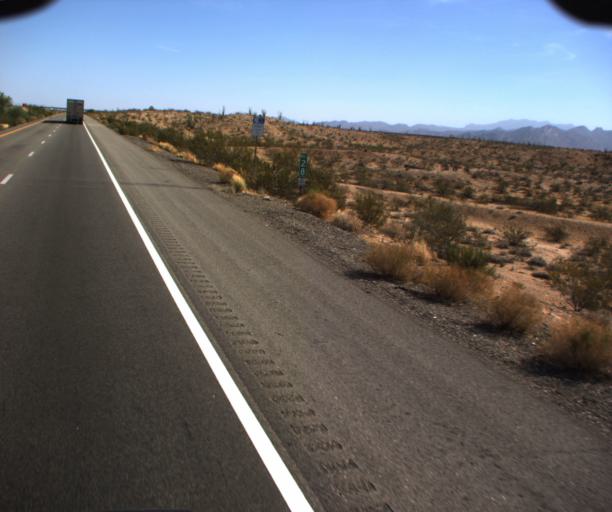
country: US
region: Arizona
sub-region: Mohave County
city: Kingman
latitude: 34.9039
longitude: -114.1543
